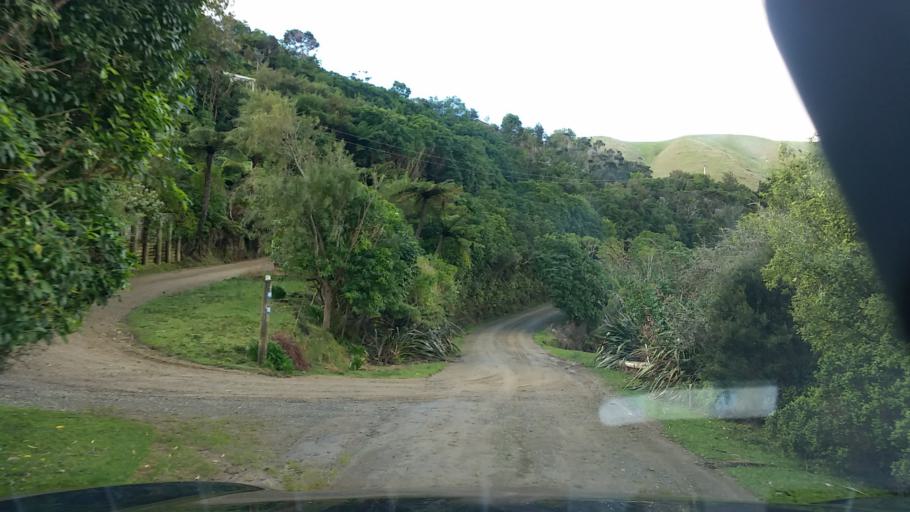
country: NZ
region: Marlborough
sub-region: Marlborough District
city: Picton
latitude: -40.9896
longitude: 173.8242
